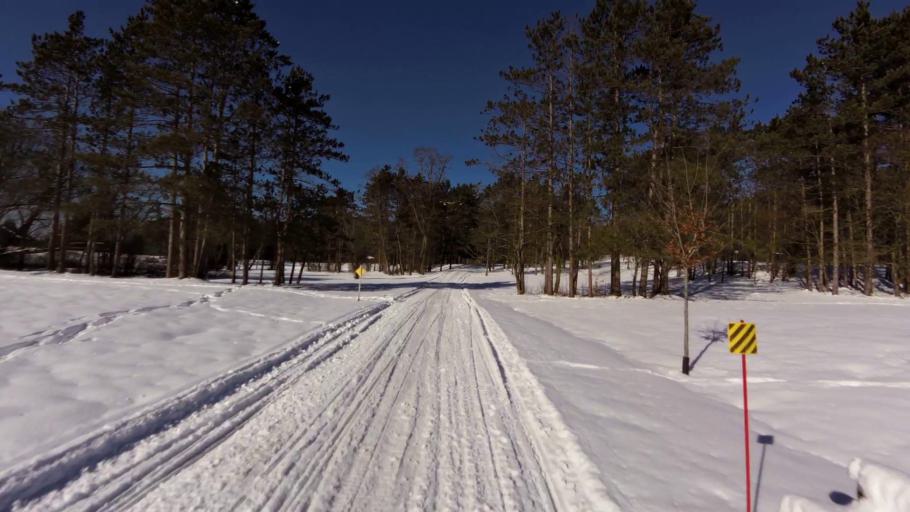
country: US
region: New York
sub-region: Cattaraugus County
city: Salamanca
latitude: 42.1069
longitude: -78.7450
